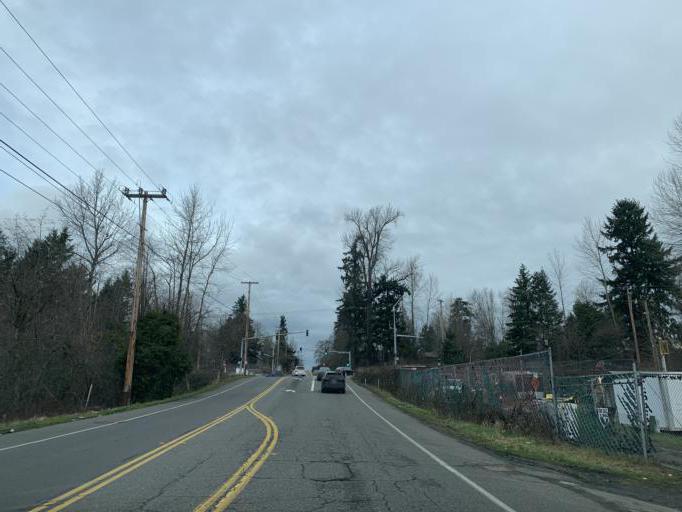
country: US
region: Washington
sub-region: King County
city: Lea Hill
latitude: 47.3622
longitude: -122.1762
